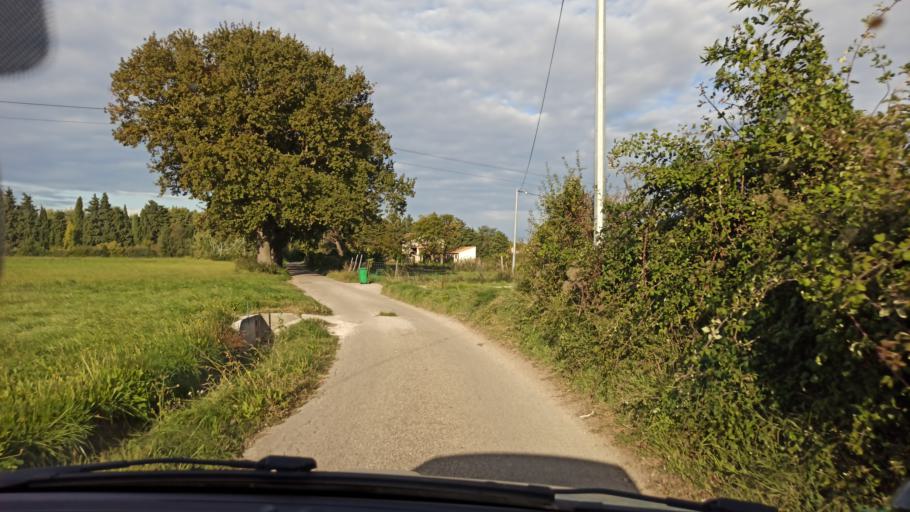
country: FR
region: Provence-Alpes-Cote d'Azur
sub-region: Departement du Vaucluse
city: Montfavet
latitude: 43.9405
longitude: 4.8582
